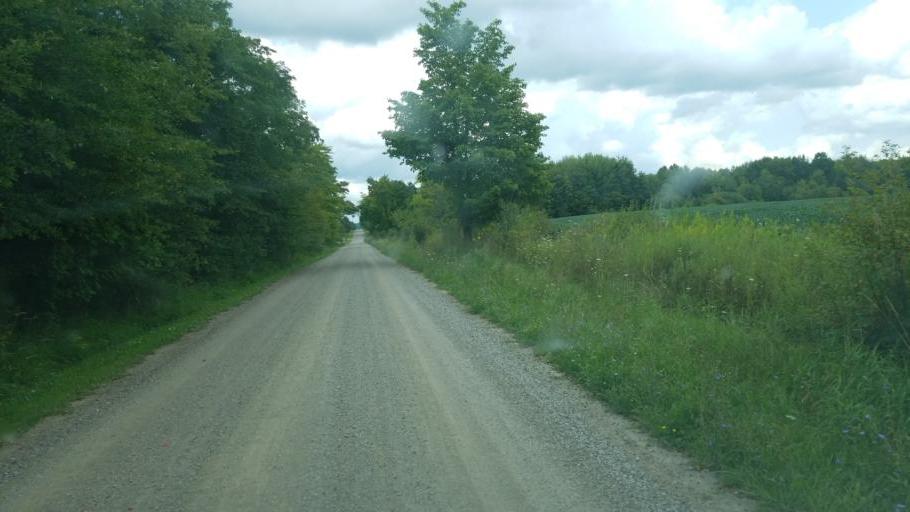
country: US
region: Ohio
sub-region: Ashtabula County
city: Andover
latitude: 41.5917
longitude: -80.6851
